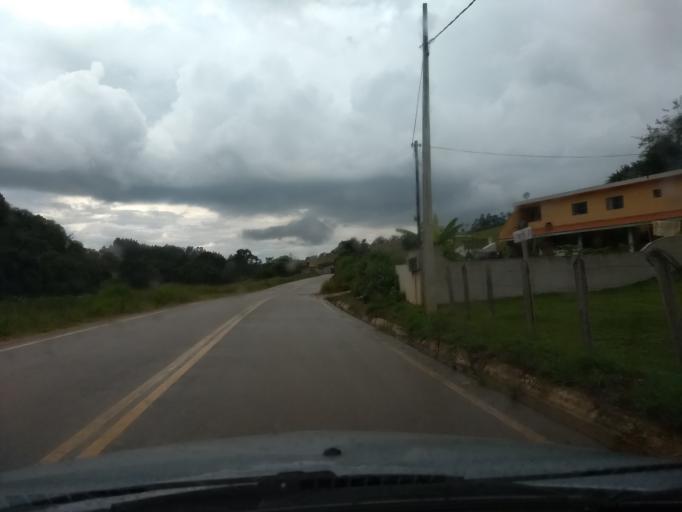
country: BR
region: Minas Gerais
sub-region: Extrema
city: Extrema
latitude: -22.7608
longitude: -46.3376
